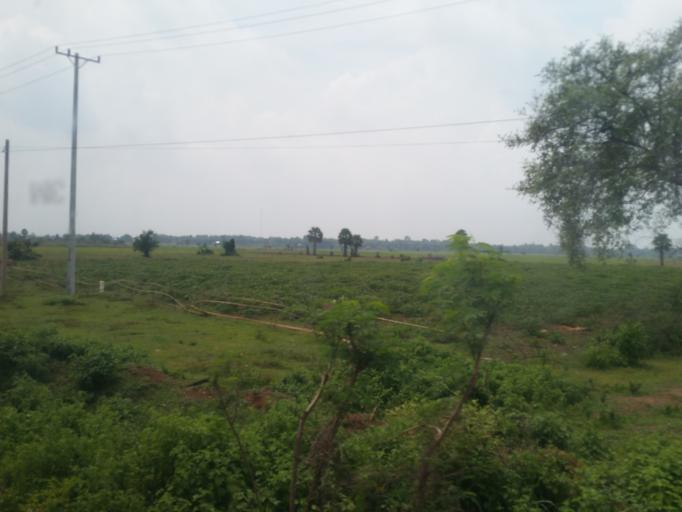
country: KH
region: Kampong Cham
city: Kampong Cham
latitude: 11.8930
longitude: 105.7983
